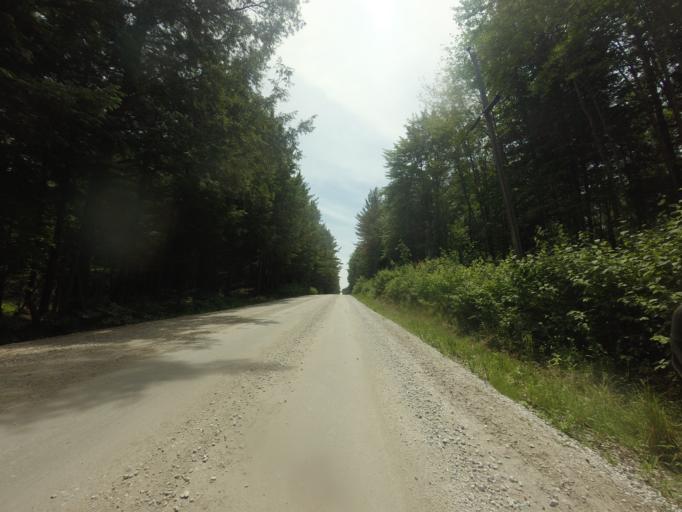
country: CA
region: Quebec
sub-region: Outaouais
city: Wakefield
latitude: 45.9601
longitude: -76.0606
